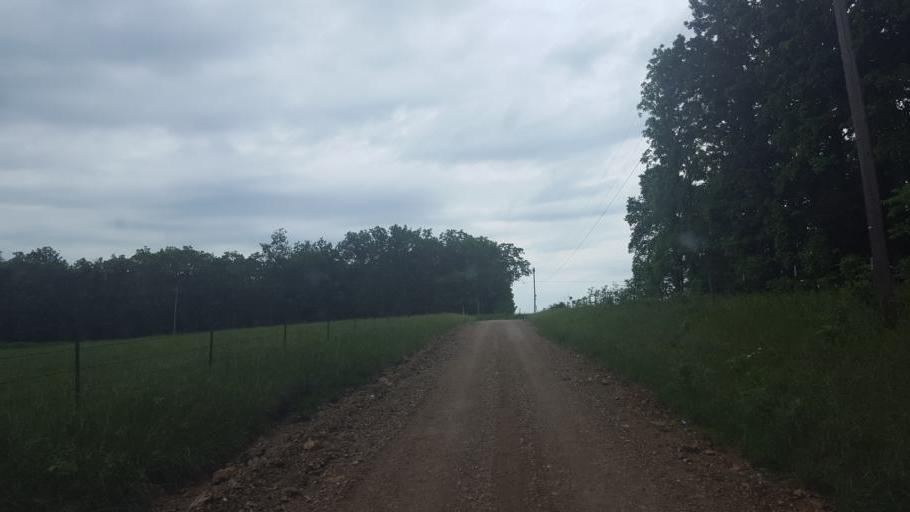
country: US
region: Missouri
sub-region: Moniteau County
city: California
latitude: 38.6734
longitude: -92.5987
